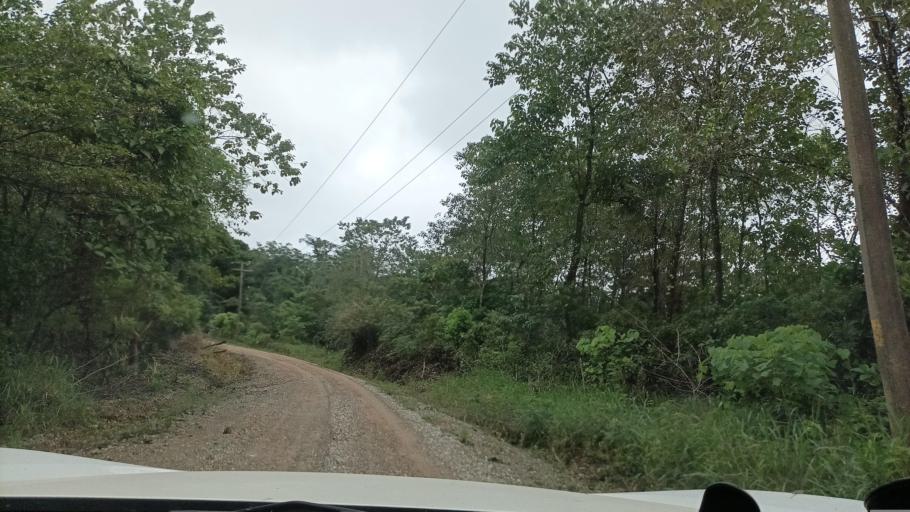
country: MX
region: Veracruz
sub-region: Uxpanapa
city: Poblado 10
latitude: 17.4215
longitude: -94.4172
